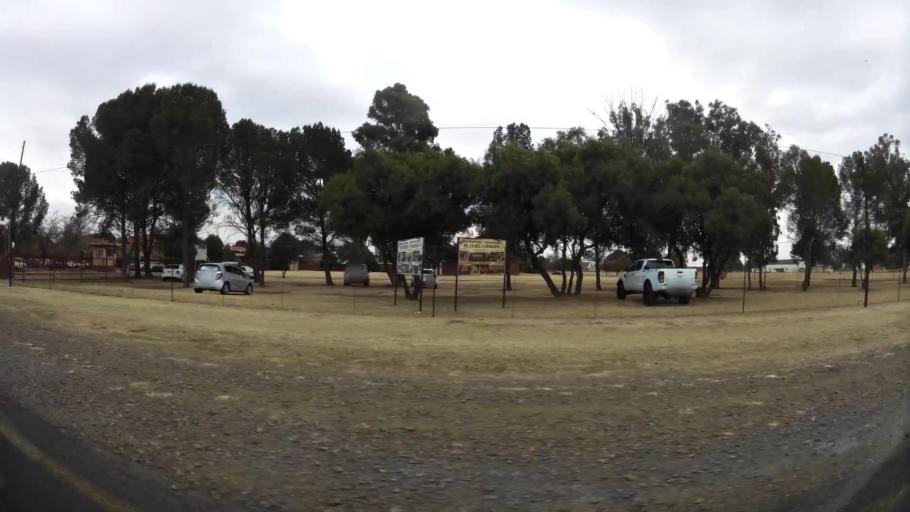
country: ZA
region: Orange Free State
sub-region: Fezile Dabi District Municipality
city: Kroonstad
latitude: -27.6223
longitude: 27.2332
